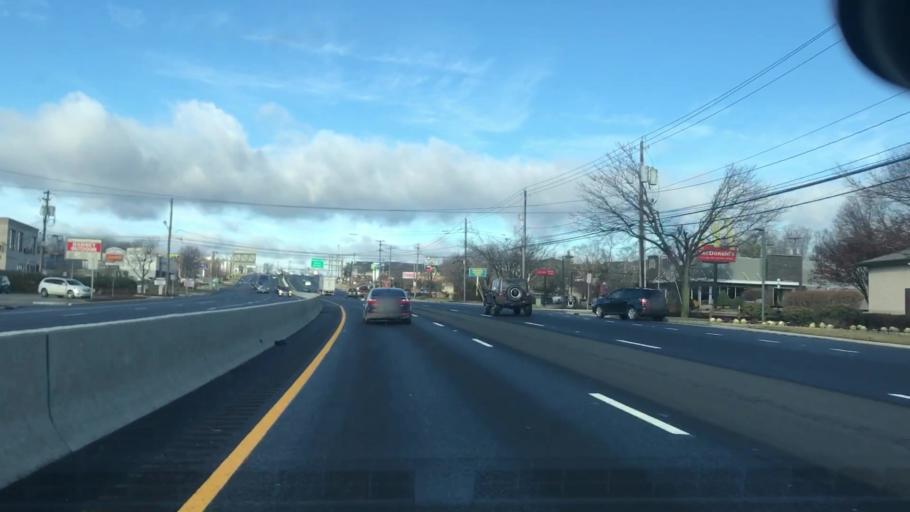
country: US
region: New Jersey
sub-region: Bergen County
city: Ramsey
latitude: 41.0635
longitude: -74.1266
